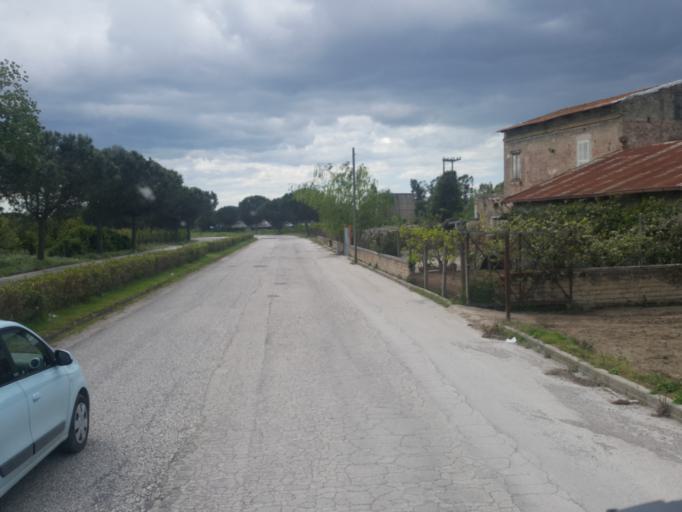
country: IT
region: Campania
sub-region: Provincia di Napoli
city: Torretta-Scalzapecora
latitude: 40.9347
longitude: 14.1165
